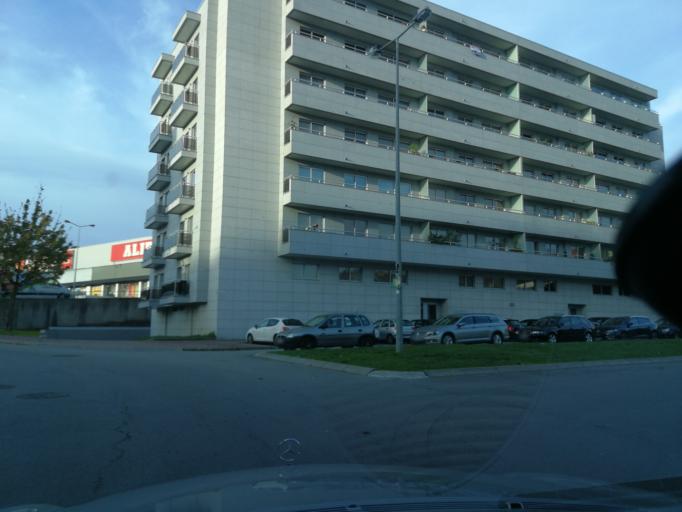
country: PT
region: Braga
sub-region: Braga
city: Braga
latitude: 41.5417
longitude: -8.4064
